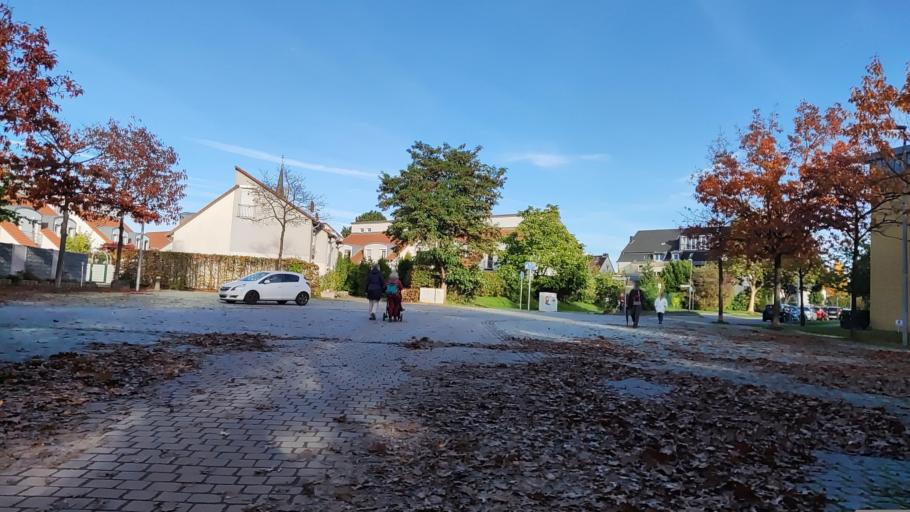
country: DE
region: North Rhine-Westphalia
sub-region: Regierungsbezirk Arnsberg
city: Herne
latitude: 51.5419
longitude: 7.2565
